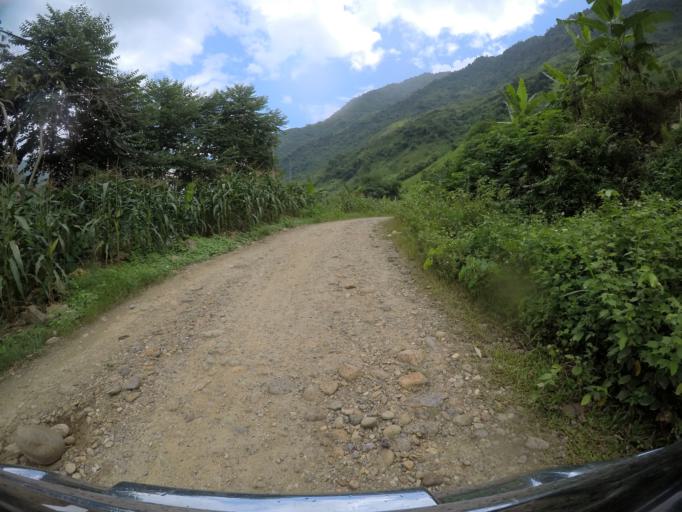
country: VN
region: Yen Bai
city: Son Thinh
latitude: 21.6697
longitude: 104.5212
